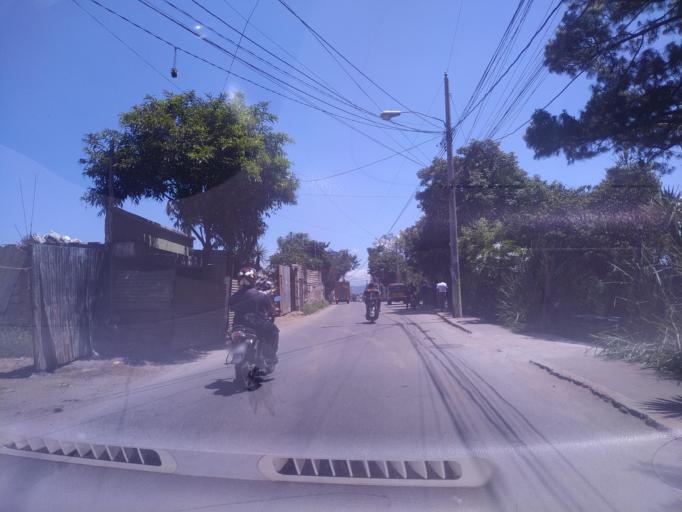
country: GT
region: Guatemala
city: Mixco
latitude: 14.6751
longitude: -90.5705
